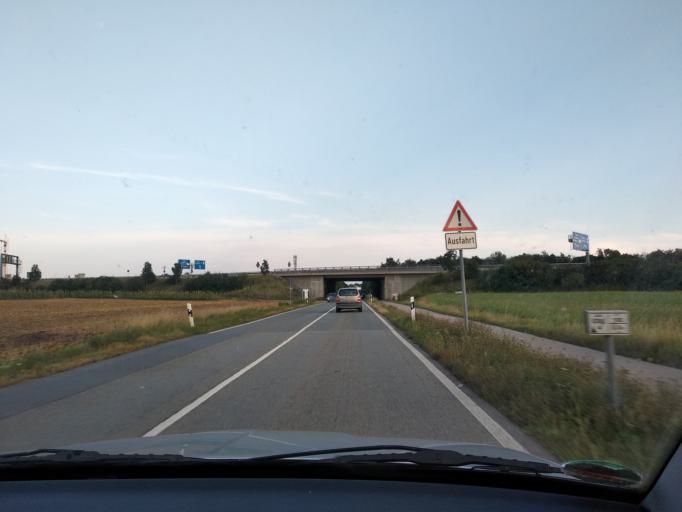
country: DE
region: Bavaria
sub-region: Upper Bavaria
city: Feldkirchen
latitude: 48.1439
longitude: 11.7525
